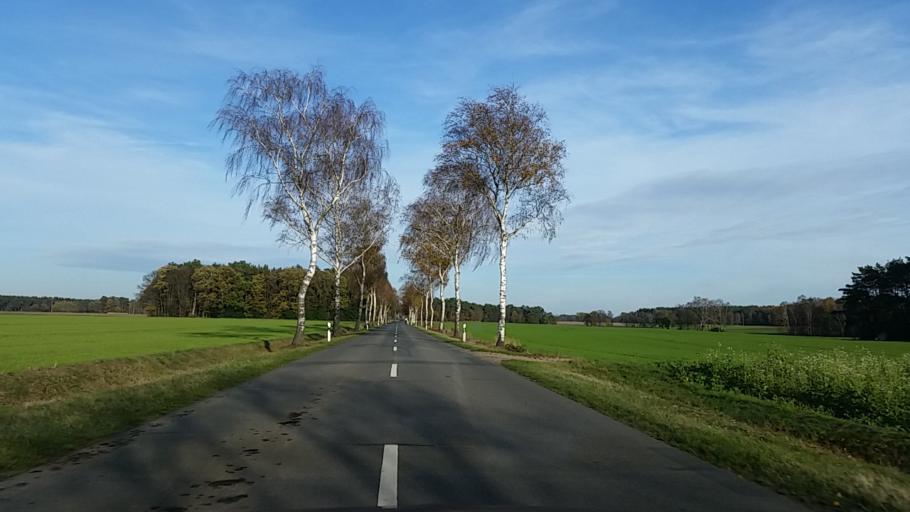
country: DE
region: Lower Saxony
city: Gross Oesingen
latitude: 52.6623
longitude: 10.5024
